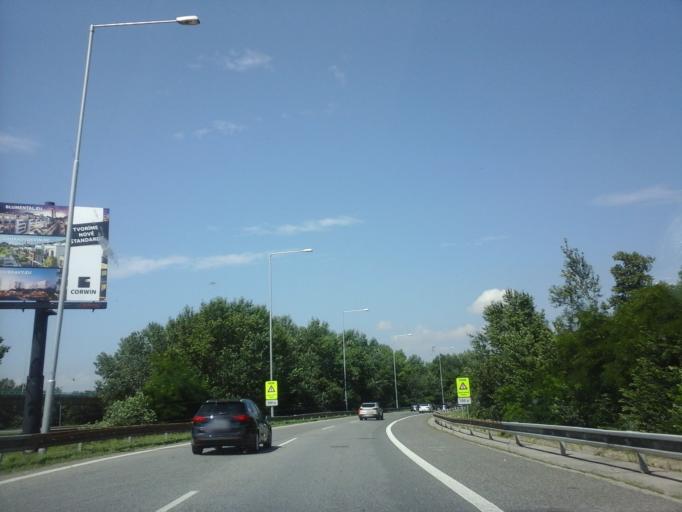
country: SK
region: Bratislavsky
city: Bratislava
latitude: 48.1278
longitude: 17.0786
